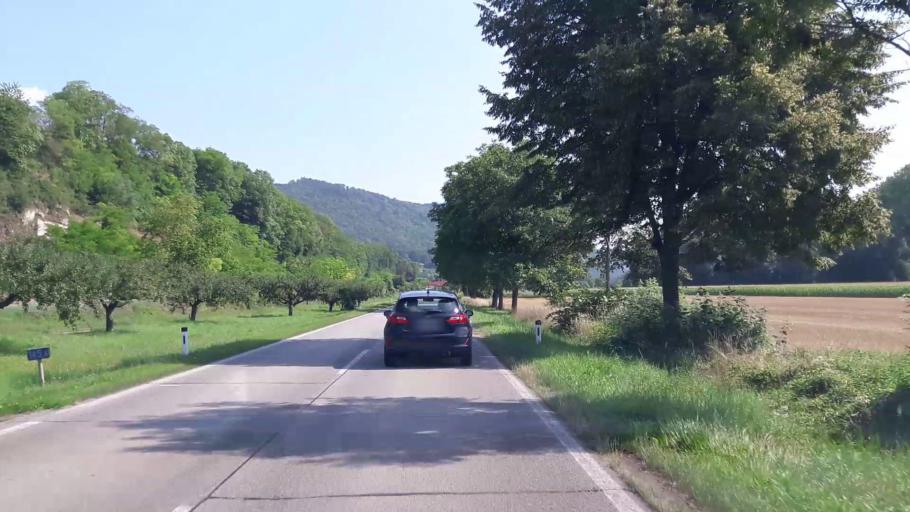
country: AT
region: Lower Austria
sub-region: Politischer Bezirk Melk
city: Emmersdorf an der Donau
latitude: 48.2572
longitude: 15.3596
